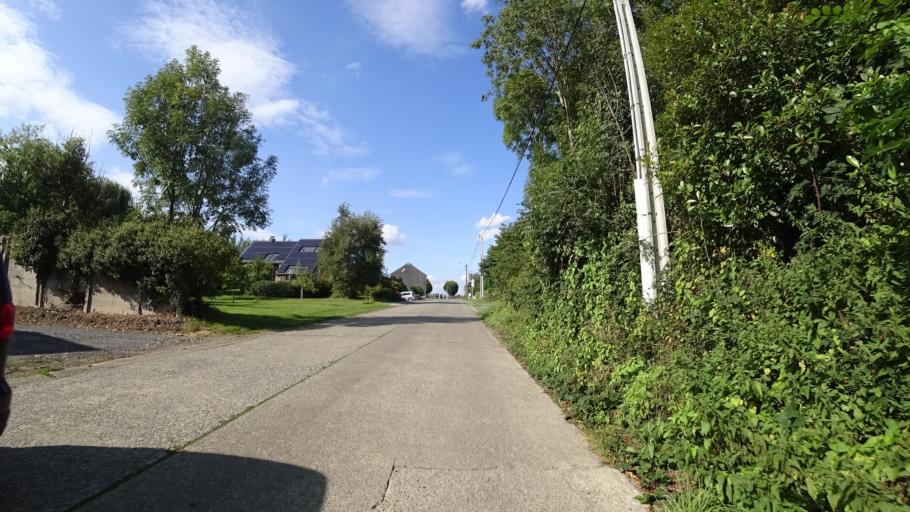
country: BE
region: Wallonia
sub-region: Province de Namur
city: Gembloux
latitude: 50.5366
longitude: 4.6537
